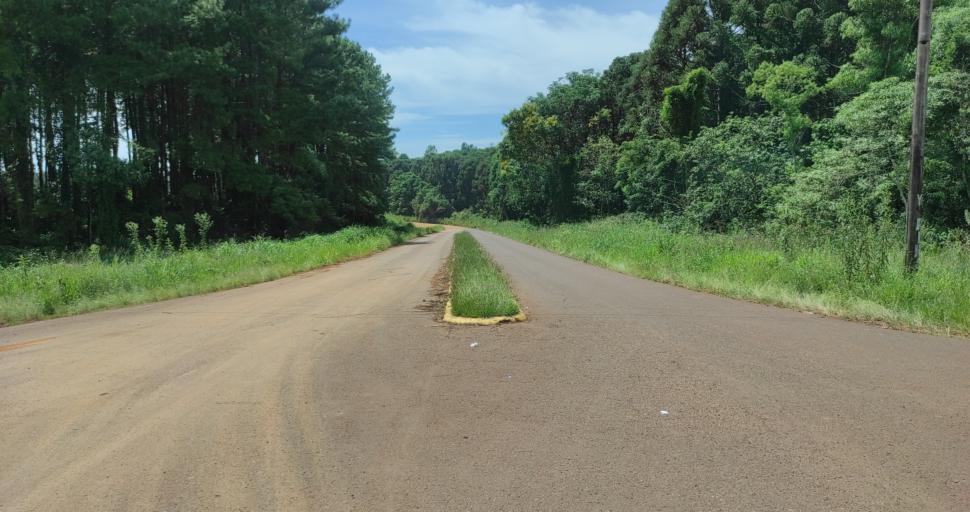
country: AR
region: Misiones
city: Puerto Piray
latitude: -26.4925
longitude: -54.6745
